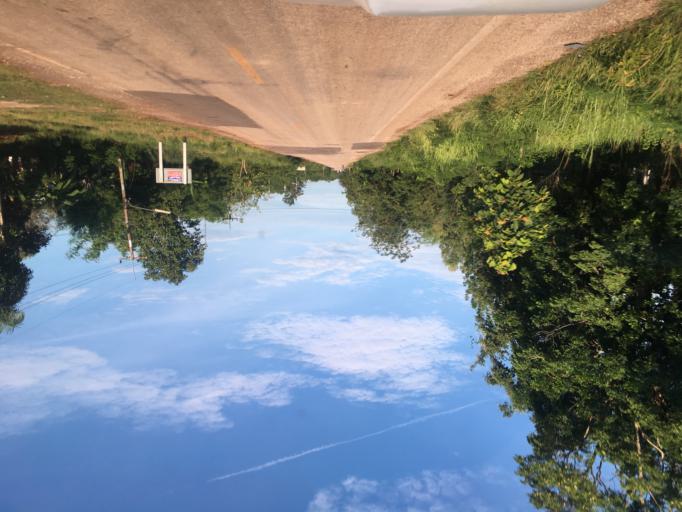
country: TH
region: Changwat Udon Thani
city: Kut Chap
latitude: 17.3834
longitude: 102.6153
